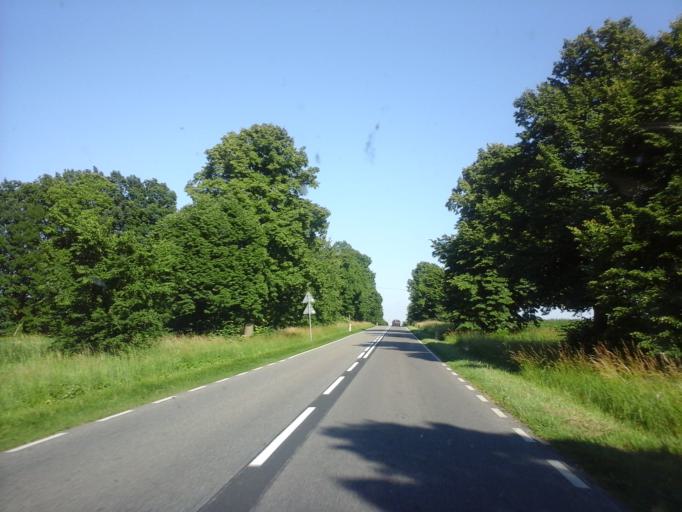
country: PL
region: West Pomeranian Voivodeship
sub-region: Powiat goleniowski
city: Nowogard
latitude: 53.6584
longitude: 15.1839
